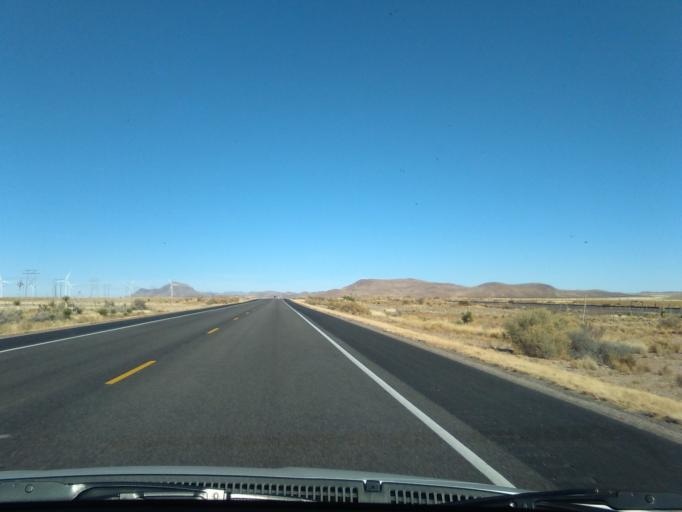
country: US
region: New Mexico
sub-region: Luna County
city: Deming
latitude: 32.4998
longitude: -107.5132
